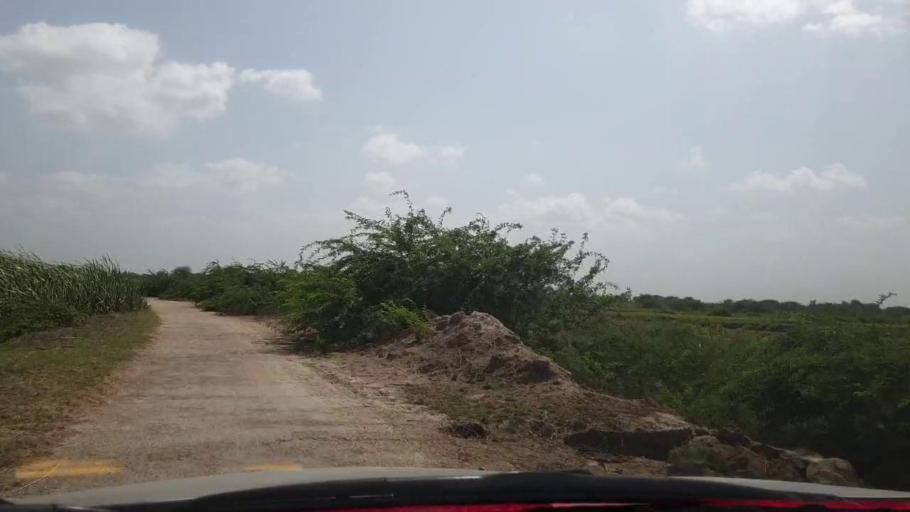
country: PK
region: Sindh
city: Tando Bago
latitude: 24.8638
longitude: 68.9198
